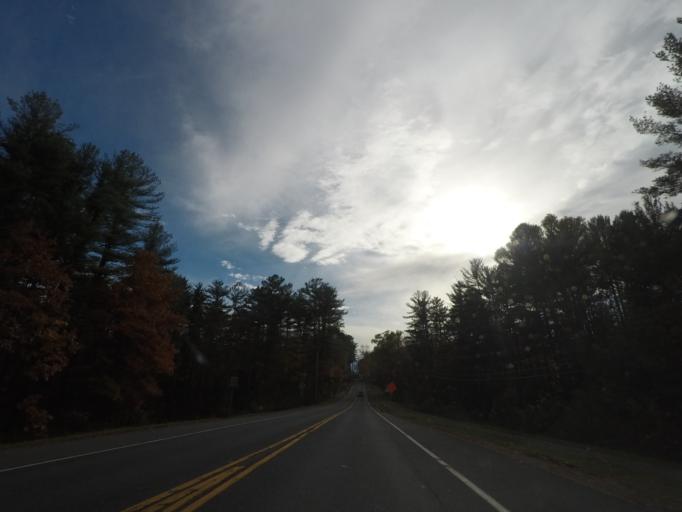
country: US
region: New York
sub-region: Albany County
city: Delmar
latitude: 42.6355
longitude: -73.8568
